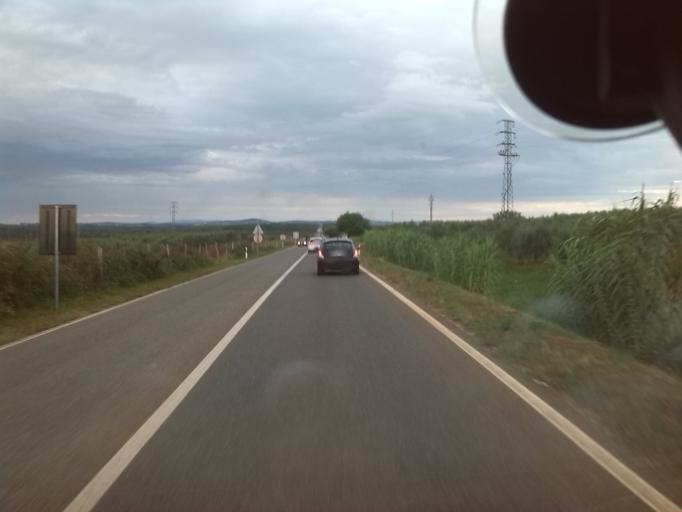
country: HR
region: Istarska
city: Novigrad
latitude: 45.3449
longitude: 13.5955
